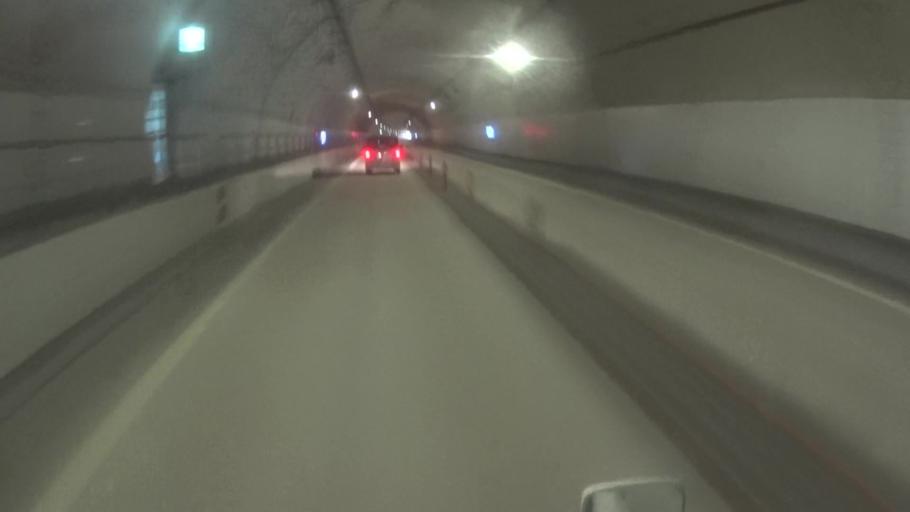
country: JP
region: Kyoto
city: Miyazu
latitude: 35.5238
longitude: 135.1800
